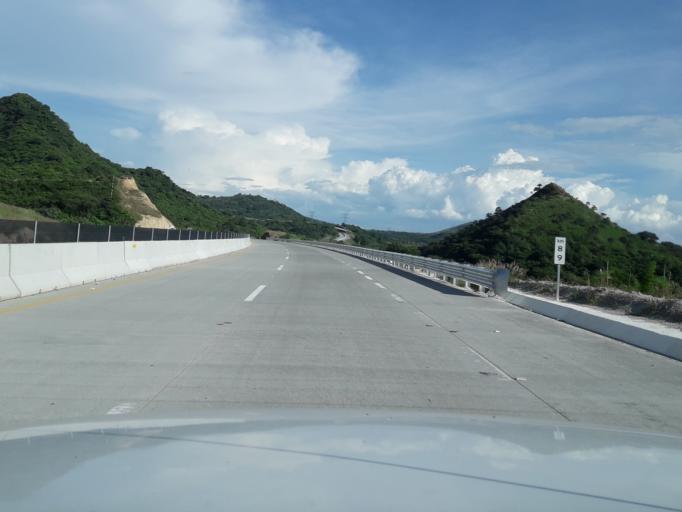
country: MX
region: Jalisco
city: Tala
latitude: 20.6003
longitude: -103.6764
